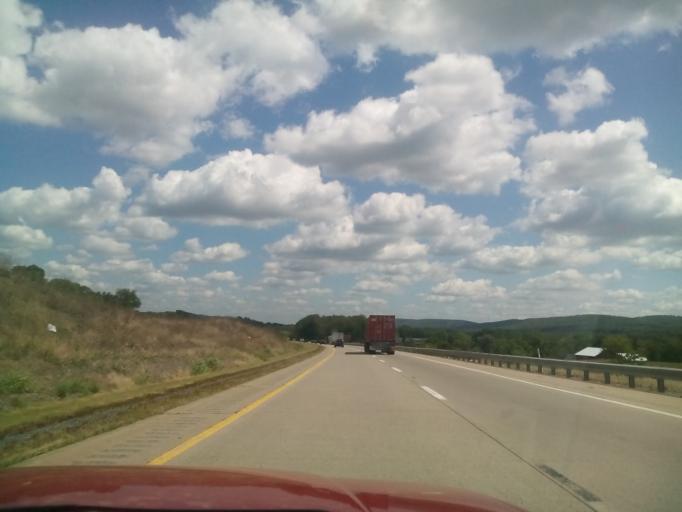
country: US
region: Pennsylvania
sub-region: Northumberland County
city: Riverside
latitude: 40.9874
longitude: -76.6945
